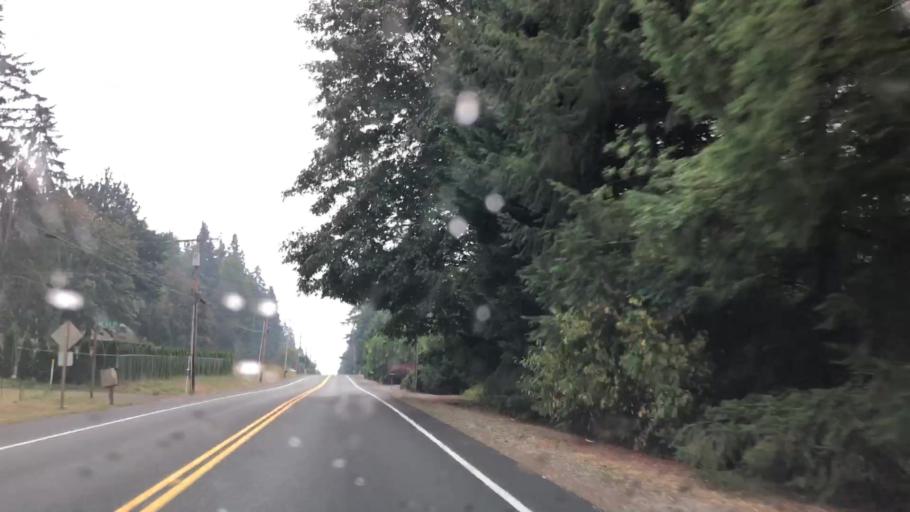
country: US
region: Washington
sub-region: King County
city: Cottage Lake
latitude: 47.7470
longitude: -122.0489
